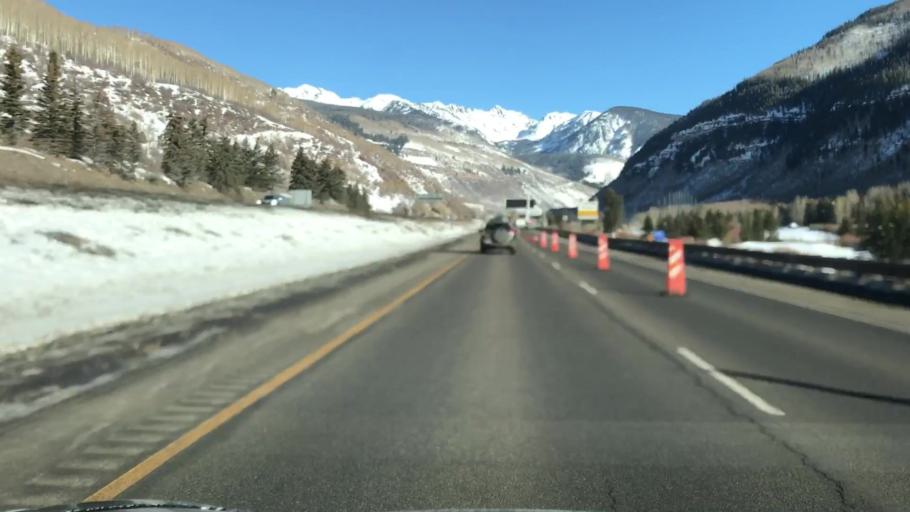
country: US
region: Colorado
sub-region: Eagle County
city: Vail
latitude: 39.6418
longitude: -106.3560
